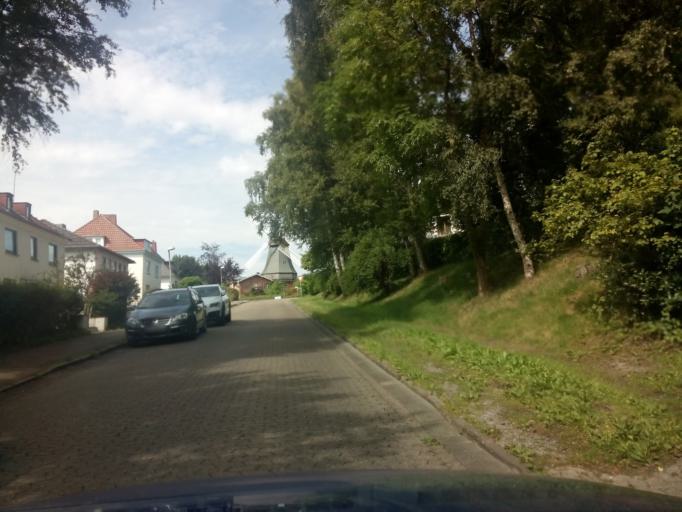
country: DE
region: Lower Saxony
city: Osterholz-Scharmbeck
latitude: 53.2280
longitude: 8.7905
